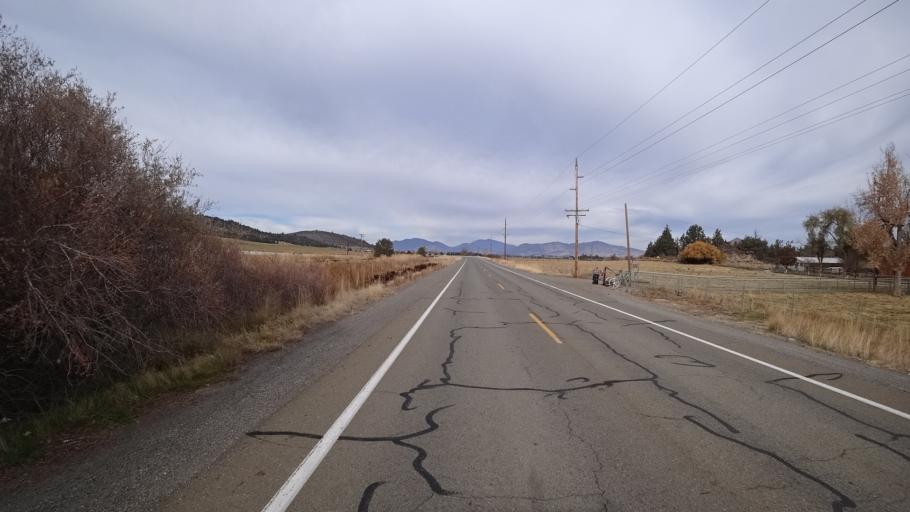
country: US
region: California
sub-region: Siskiyou County
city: Montague
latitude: 41.6773
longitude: -122.5272
